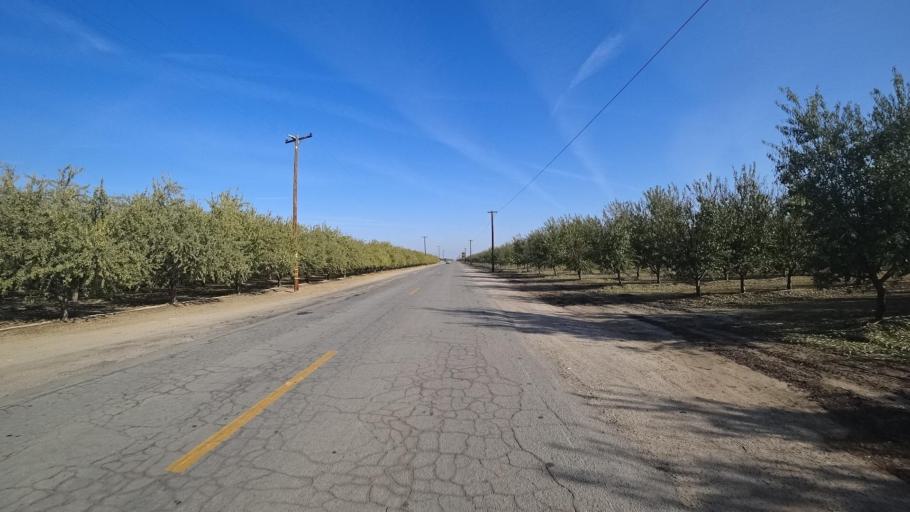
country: US
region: California
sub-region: Kern County
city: McFarland
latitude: 35.7032
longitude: -119.3252
